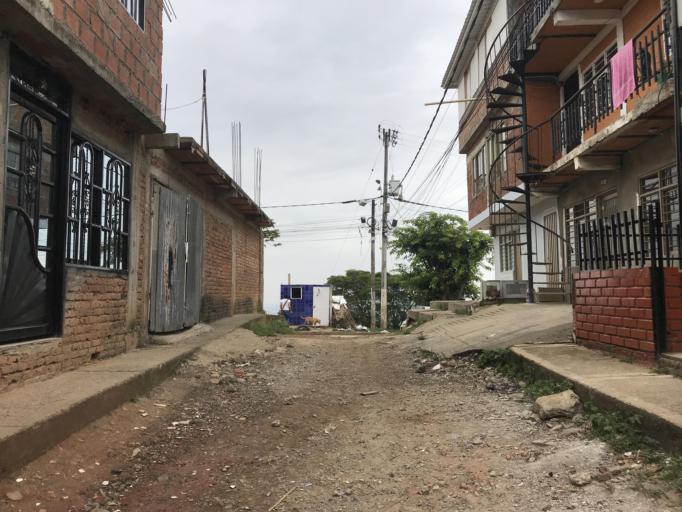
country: CO
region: Valle del Cauca
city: Cali
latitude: 3.3741
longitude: -76.5592
